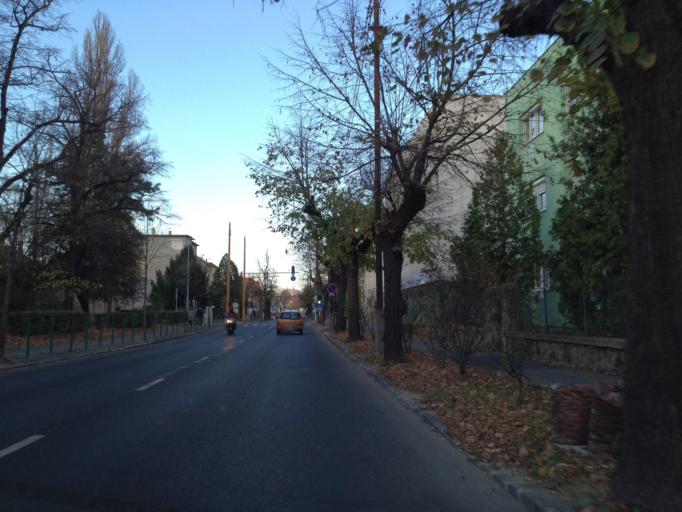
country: HU
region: Gyor-Moson-Sopron
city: Gyor
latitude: 47.6773
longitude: 17.6395
